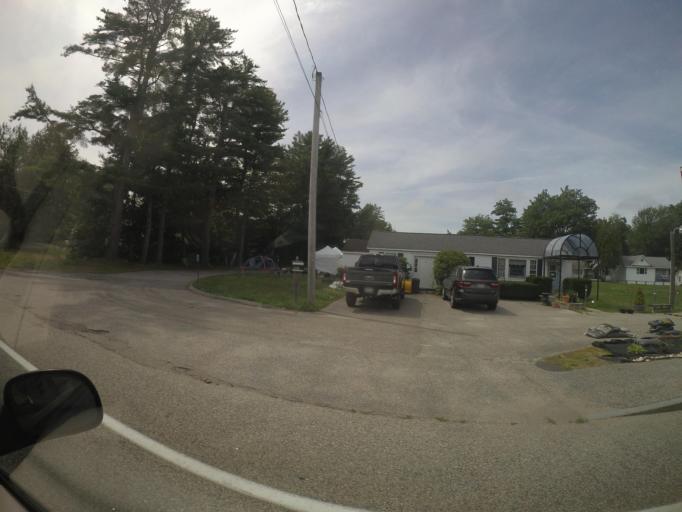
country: US
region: Maine
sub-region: Cumberland County
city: West Scarborough
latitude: 43.5499
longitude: -70.4093
